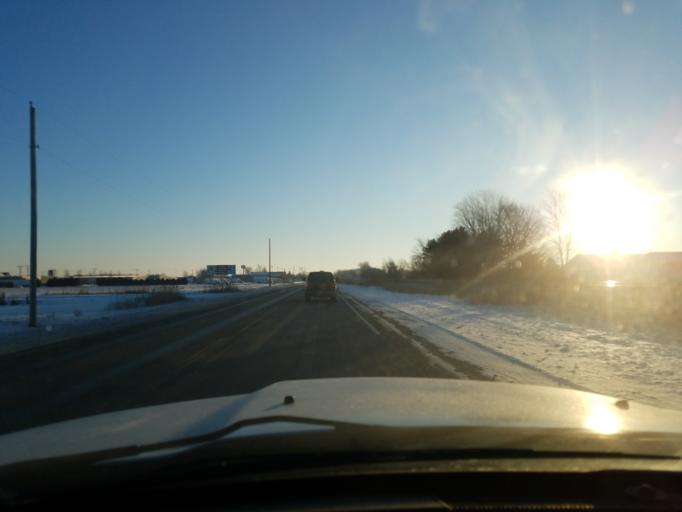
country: US
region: Indiana
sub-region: Elkhart County
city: Nappanee
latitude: 41.4441
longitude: -86.0427
